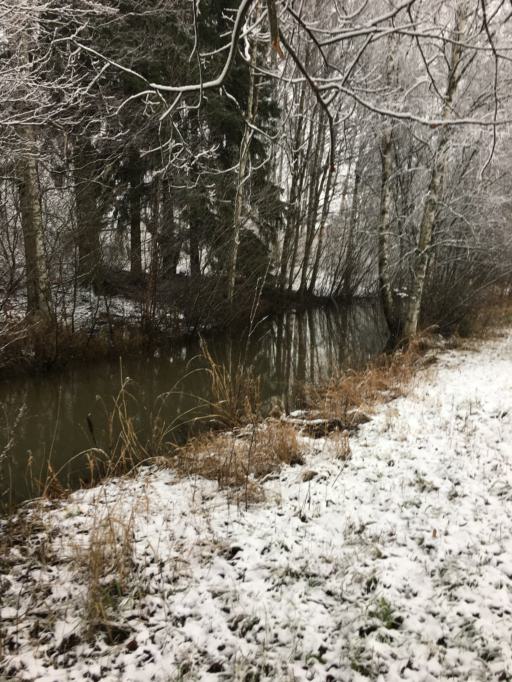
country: FI
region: Uusimaa
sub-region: Helsinki
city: Vantaa
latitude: 60.2528
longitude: 25.0297
